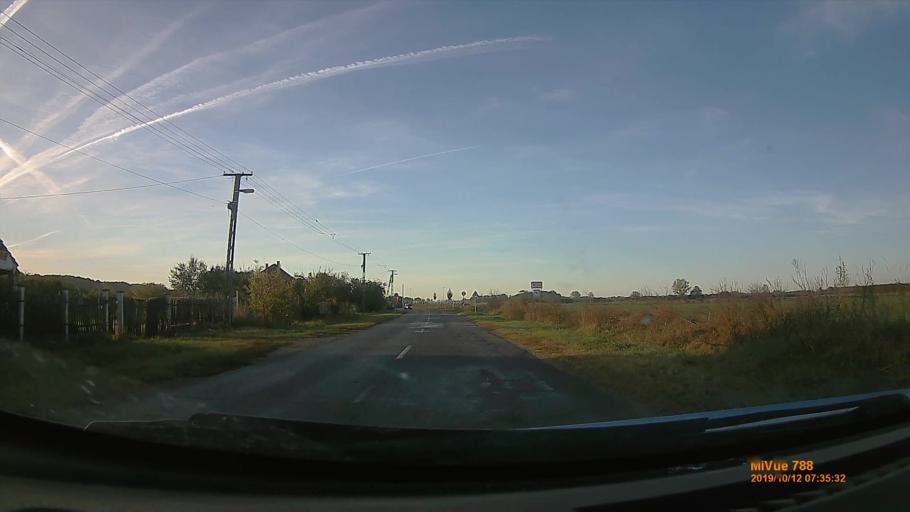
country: HU
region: Hajdu-Bihar
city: Pocsaj
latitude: 47.2529
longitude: 21.8108
